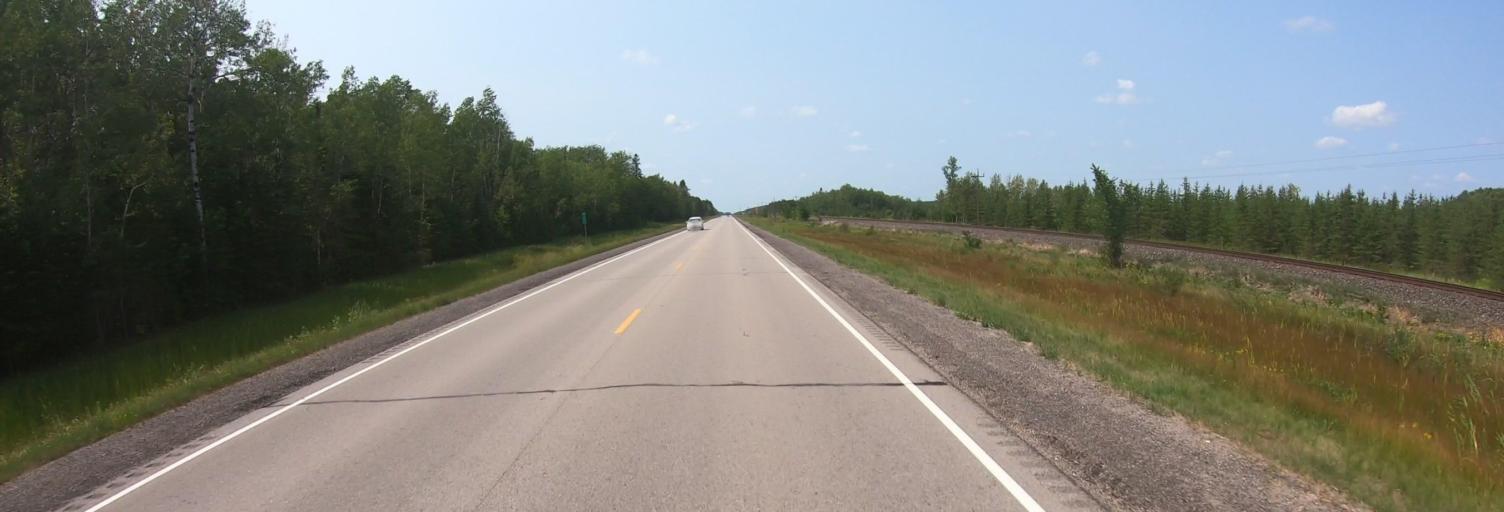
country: US
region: Minnesota
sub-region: Lake of the Woods County
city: Baudette
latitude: 48.7251
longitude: -94.7724
